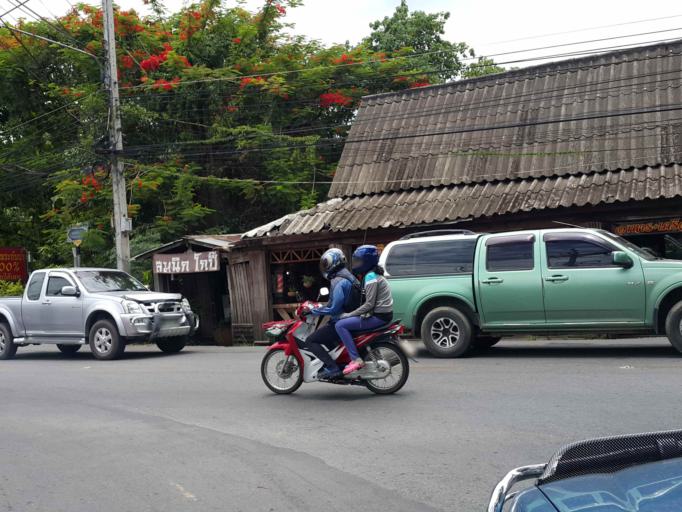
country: TH
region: Chiang Mai
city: Chiang Mai
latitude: 18.7756
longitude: 99.0080
